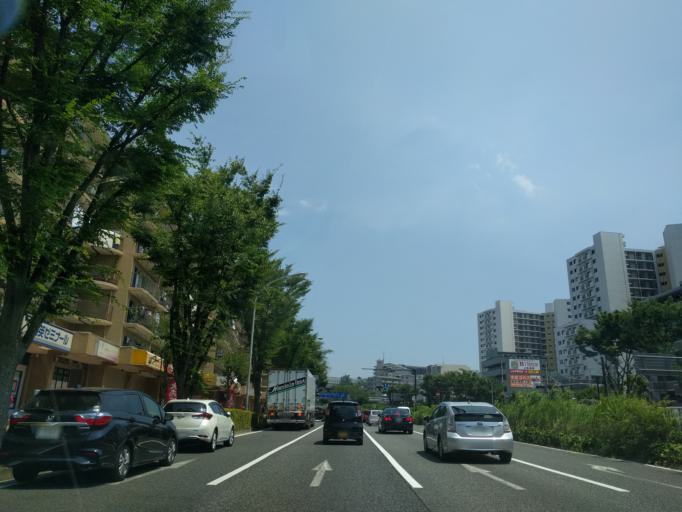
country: JP
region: Kanagawa
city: Yokohama
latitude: 35.4037
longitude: 139.5718
